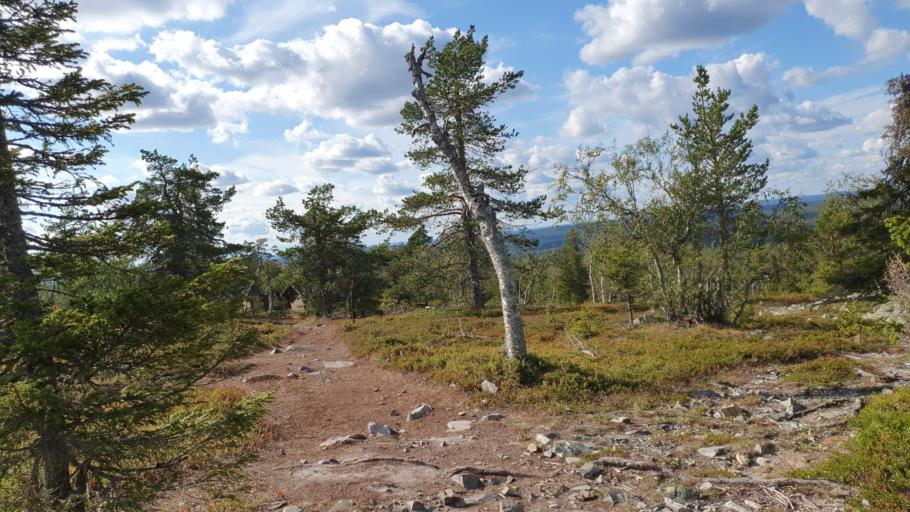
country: FI
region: Lapland
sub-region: Tunturi-Lappi
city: Kolari
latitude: 67.6151
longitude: 24.2564
